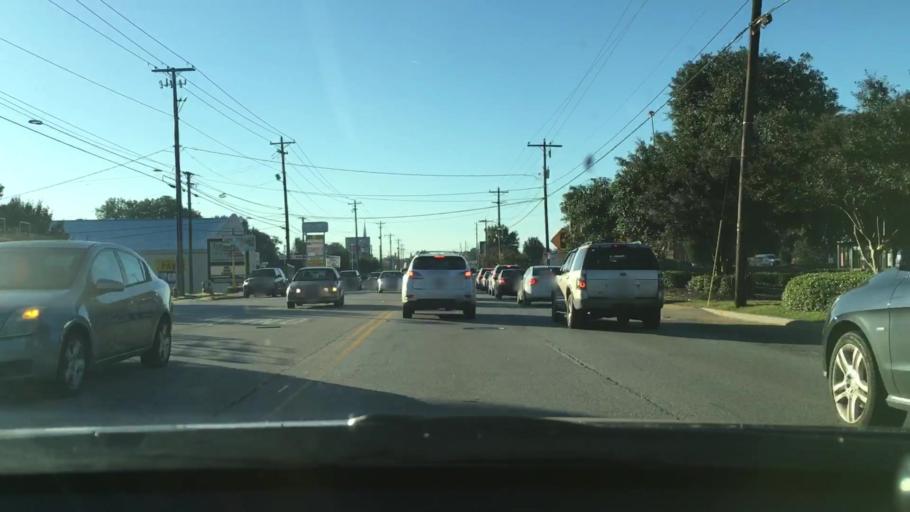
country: US
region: South Carolina
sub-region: Lexington County
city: Saint Andrews
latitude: 34.0353
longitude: -81.0893
